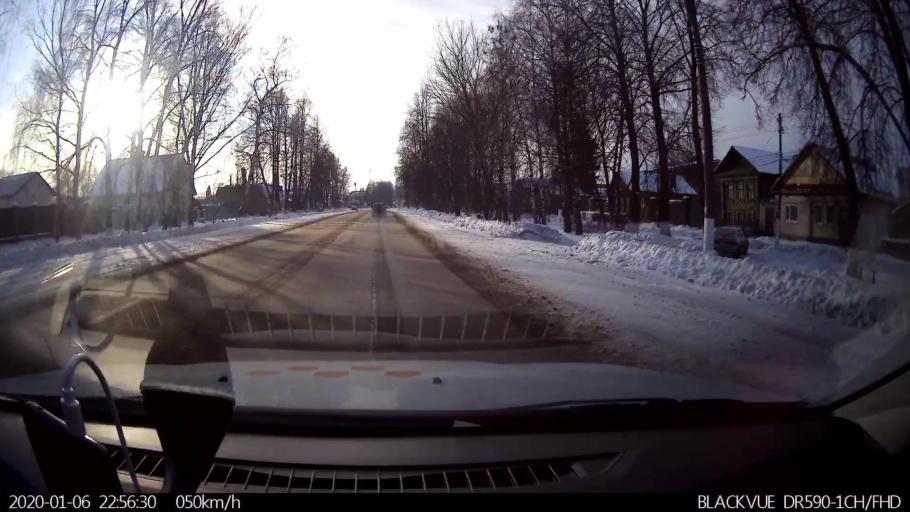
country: RU
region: Nizjnij Novgorod
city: Bogorodsk
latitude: 56.1109
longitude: 43.5311
